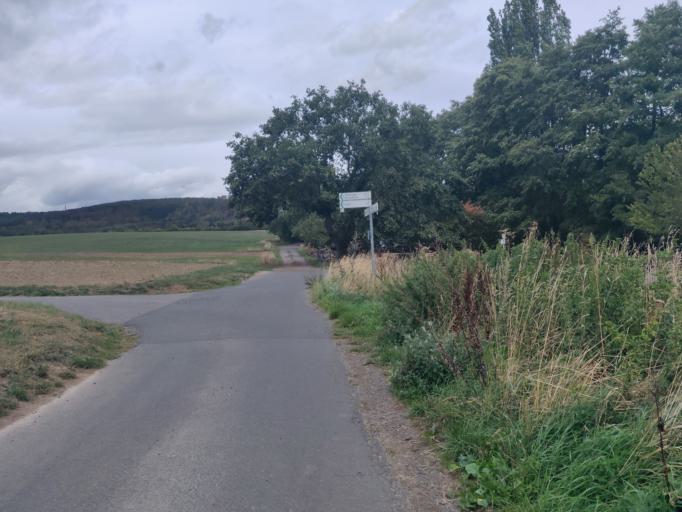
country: DE
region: Hesse
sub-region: Regierungsbezirk Kassel
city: Baunatal
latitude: 51.2843
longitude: 9.3600
